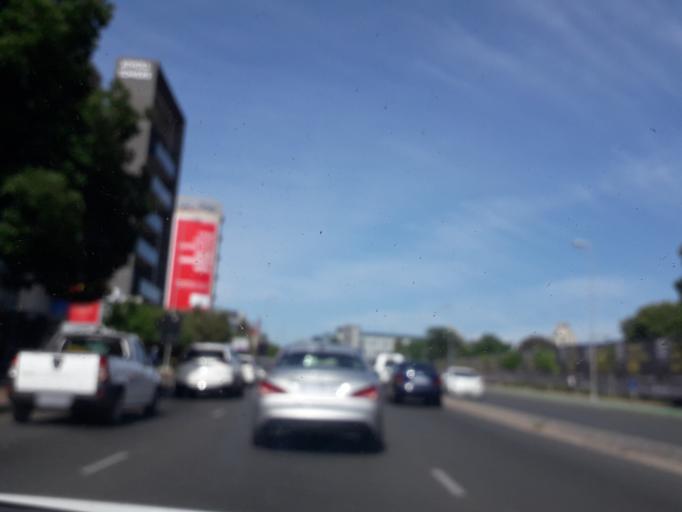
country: ZA
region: Gauteng
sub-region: City of Johannesburg Metropolitan Municipality
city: Modderfontein
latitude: -26.1050
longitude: 28.0688
